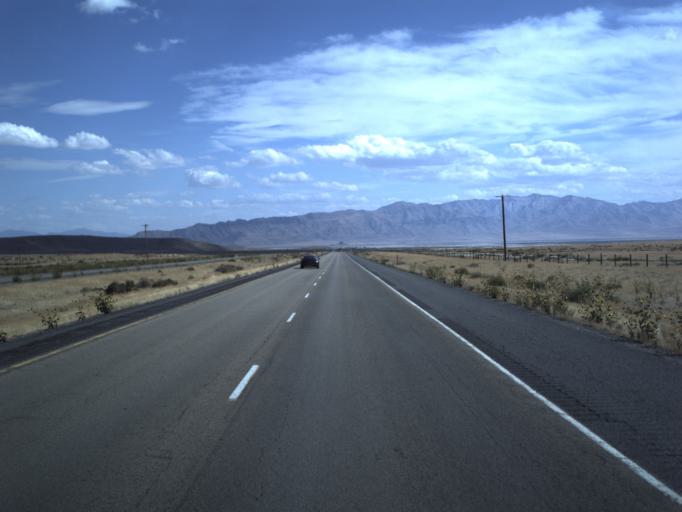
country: US
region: Utah
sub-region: Tooele County
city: Grantsville
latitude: 40.7996
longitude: -112.8489
